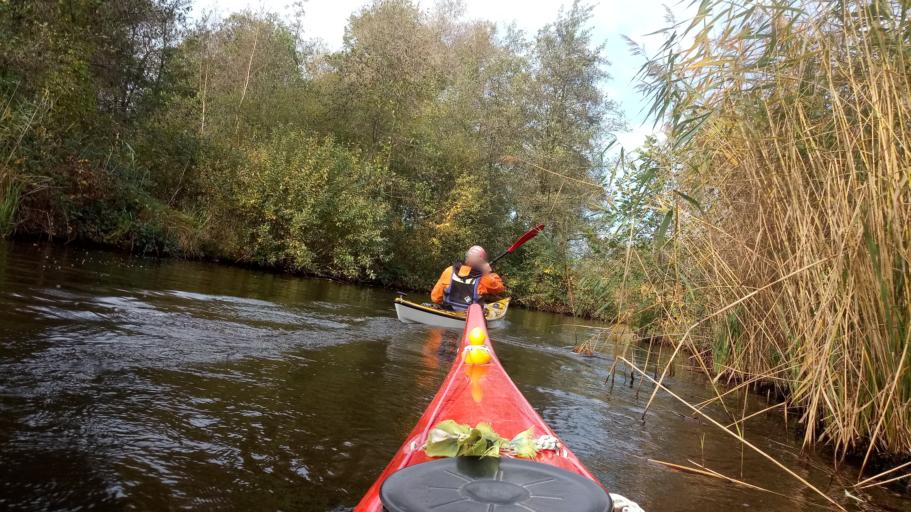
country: NL
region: Overijssel
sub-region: Gemeente Steenwijkerland
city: Sint Jansklooster
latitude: 52.6692
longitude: 6.0310
